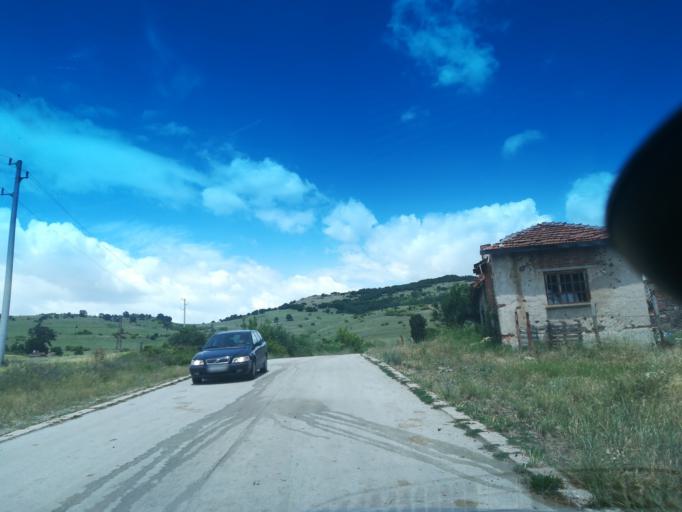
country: BG
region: Khaskovo
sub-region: Obshtina Mineralni Bani
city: Mineralni Bani
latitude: 41.9495
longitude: 25.2473
